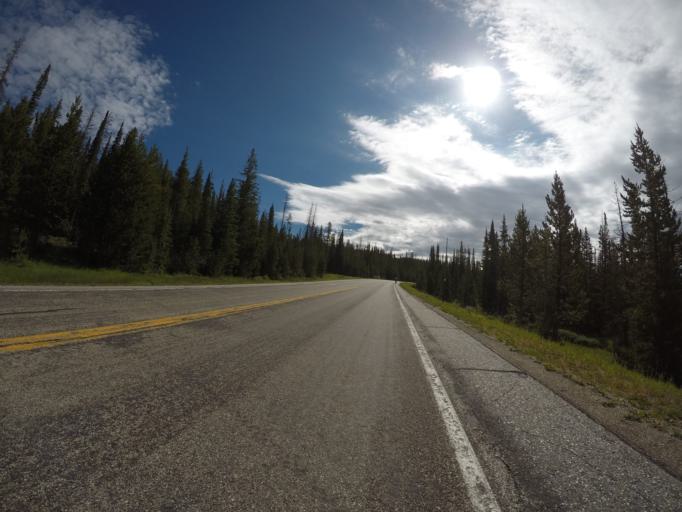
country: US
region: Wyoming
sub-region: Carbon County
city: Saratoga
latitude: 41.3262
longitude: -106.4339
